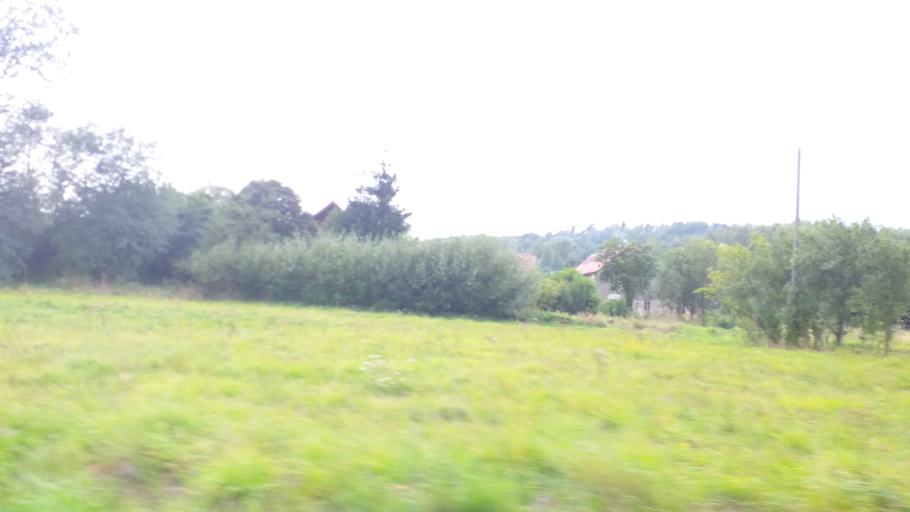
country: PL
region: Lower Silesian Voivodeship
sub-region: Powiat lubanski
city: Lesna
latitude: 51.0557
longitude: 15.2750
